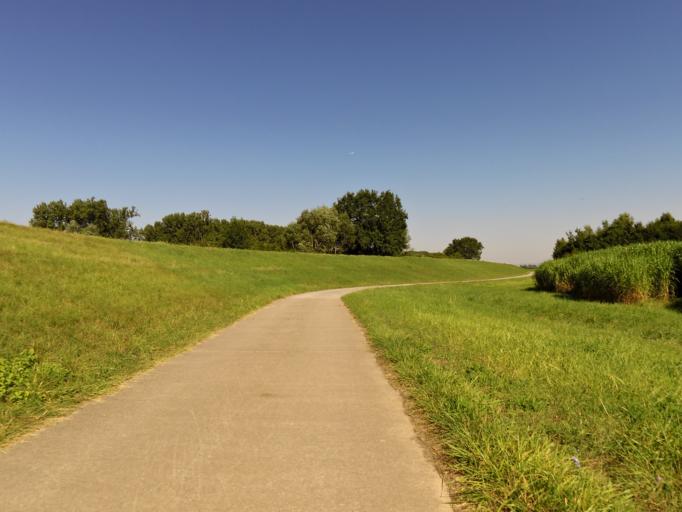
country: DE
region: Rheinland-Pfalz
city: Oppenheim
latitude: 49.8421
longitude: 8.4046
